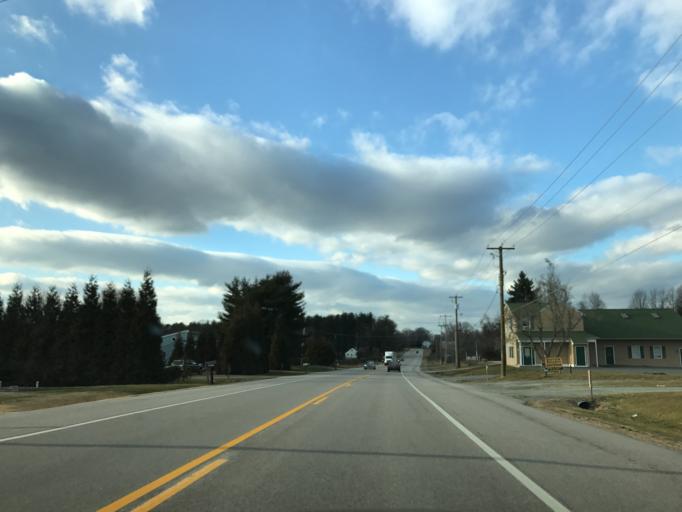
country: US
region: Maryland
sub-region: Cecil County
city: North East
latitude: 39.6489
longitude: -75.9707
